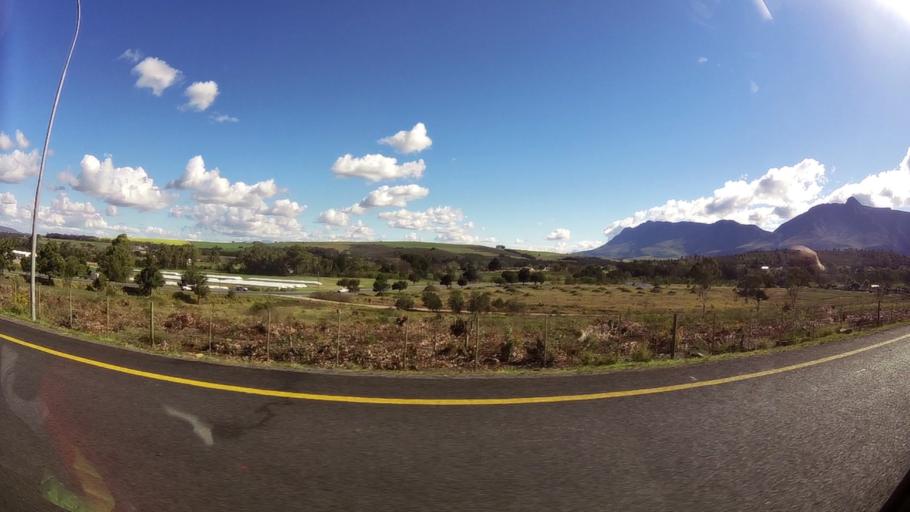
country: ZA
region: Western Cape
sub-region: Overberg District Municipality
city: Swellendam
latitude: -34.0417
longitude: 20.4314
